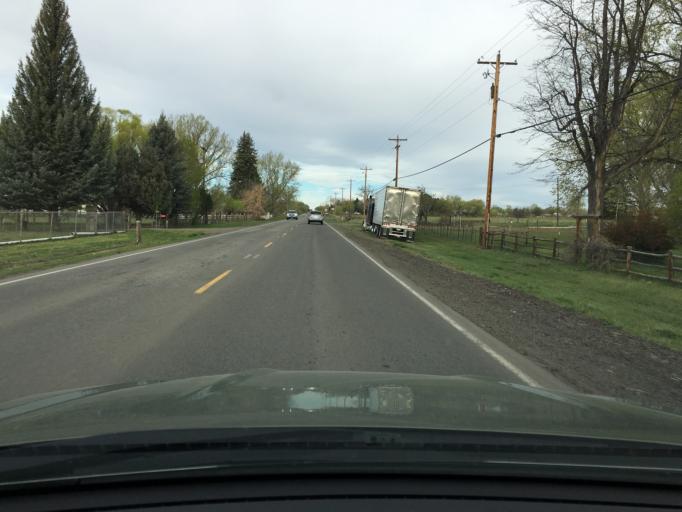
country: US
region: Colorado
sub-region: Delta County
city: Paonia
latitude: 38.7998
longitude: -107.7513
